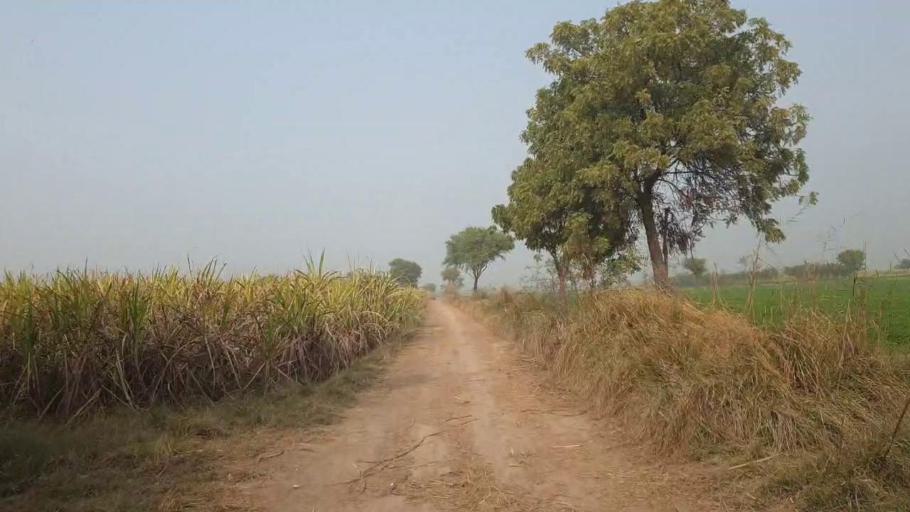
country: PK
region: Sindh
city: Tando Adam
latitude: 25.8332
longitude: 68.6003
